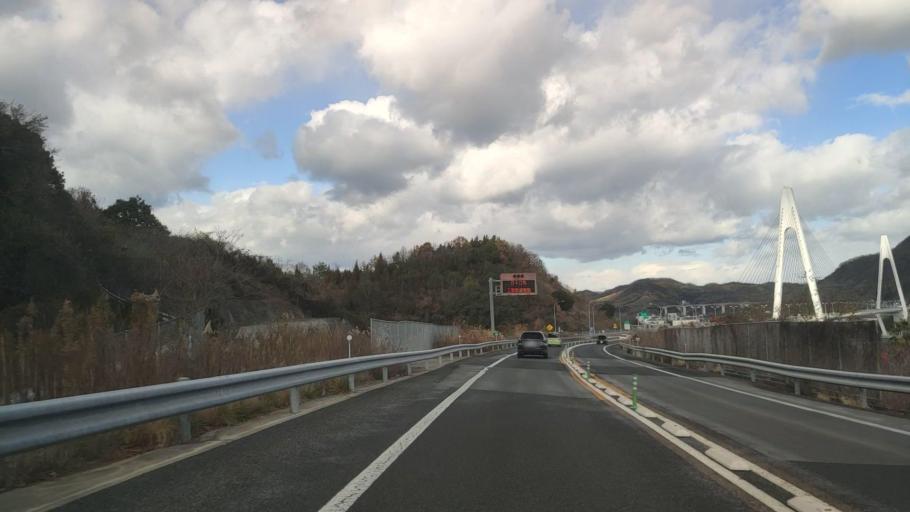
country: JP
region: Hiroshima
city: Innoshima
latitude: 34.2982
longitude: 133.1450
